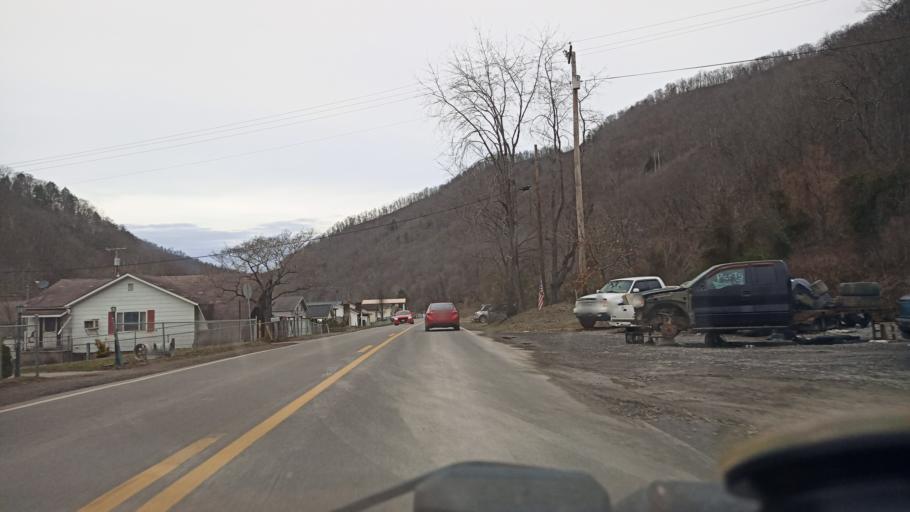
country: US
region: West Virginia
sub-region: Logan County
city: Mallory
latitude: 37.7127
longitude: -81.8676
